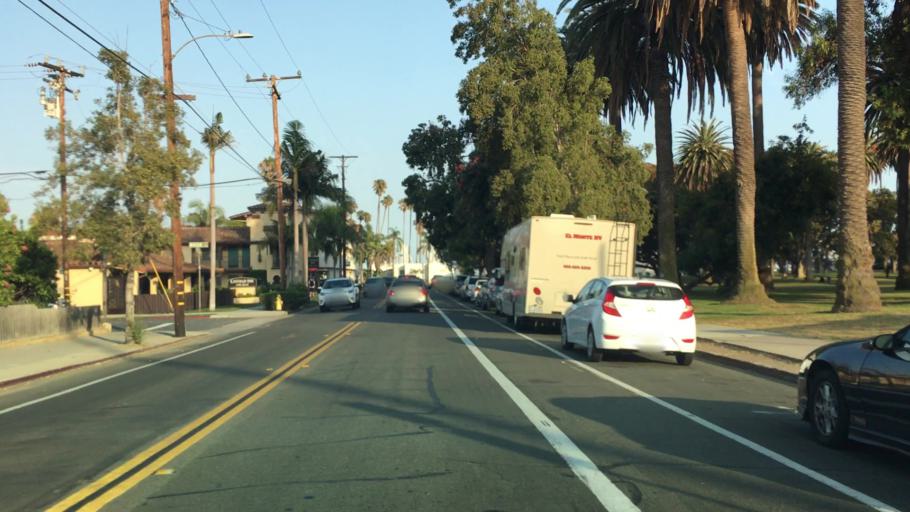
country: US
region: California
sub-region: Santa Barbara County
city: Santa Barbara
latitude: 34.4090
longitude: -119.6952
